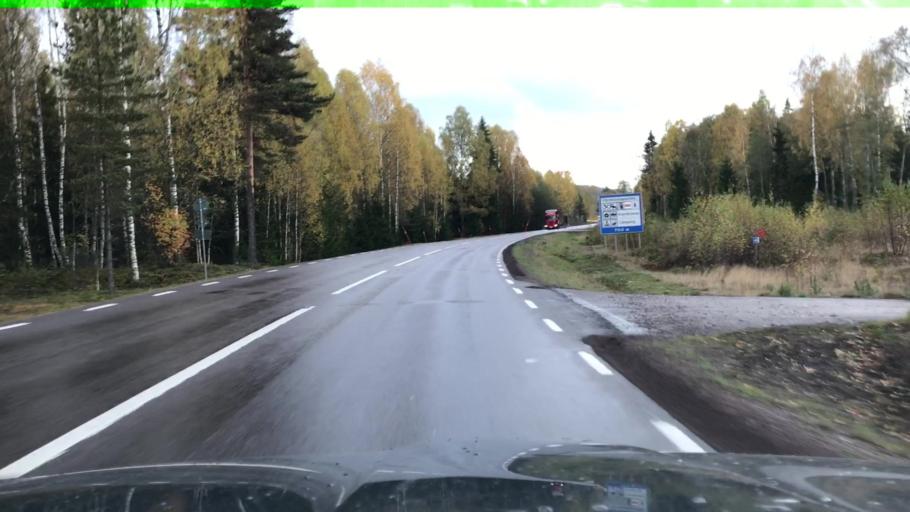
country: SE
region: Vaermland
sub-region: Hagfors Kommun
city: Ekshaerad
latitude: 60.4285
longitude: 13.2479
